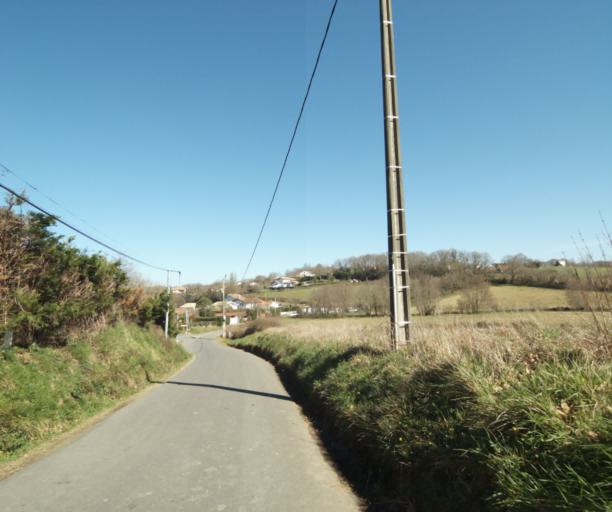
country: FR
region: Aquitaine
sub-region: Departement des Pyrenees-Atlantiques
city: Urrugne
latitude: 43.3469
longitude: -1.7170
